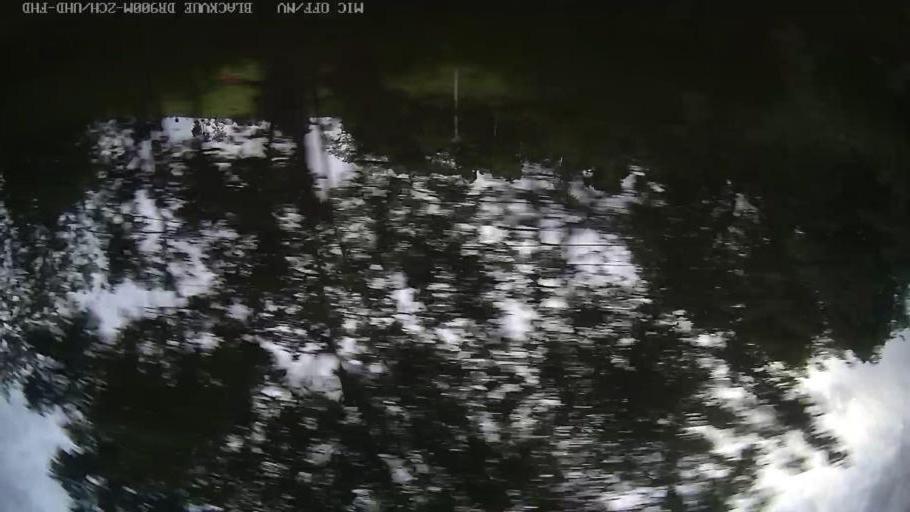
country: BR
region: Sao Paulo
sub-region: Amparo
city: Amparo
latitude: -22.8474
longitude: -46.7797
